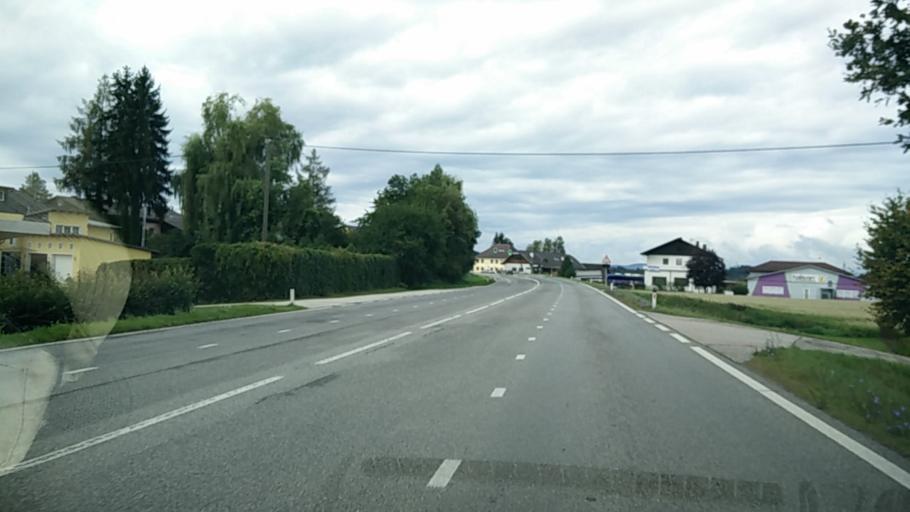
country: AT
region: Carinthia
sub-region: Politischer Bezirk Klagenfurt Land
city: Poggersdorf
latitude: 46.6407
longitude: 14.4309
